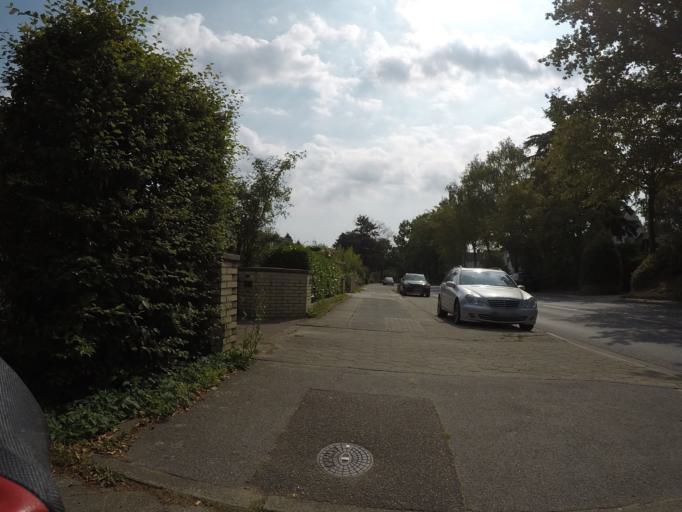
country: DE
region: Hamburg
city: Poppenbuettel
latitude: 53.6728
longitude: 10.0582
